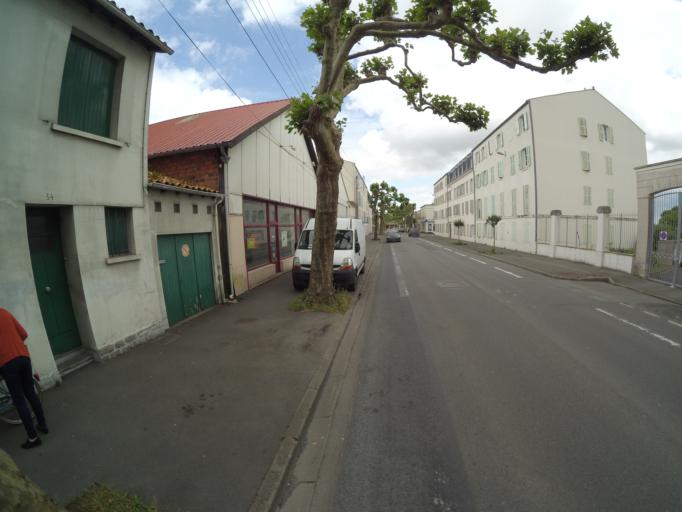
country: FR
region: Poitou-Charentes
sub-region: Departement de la Charente-Maritime
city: Rochefort
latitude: 45.9450
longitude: -0.9619
